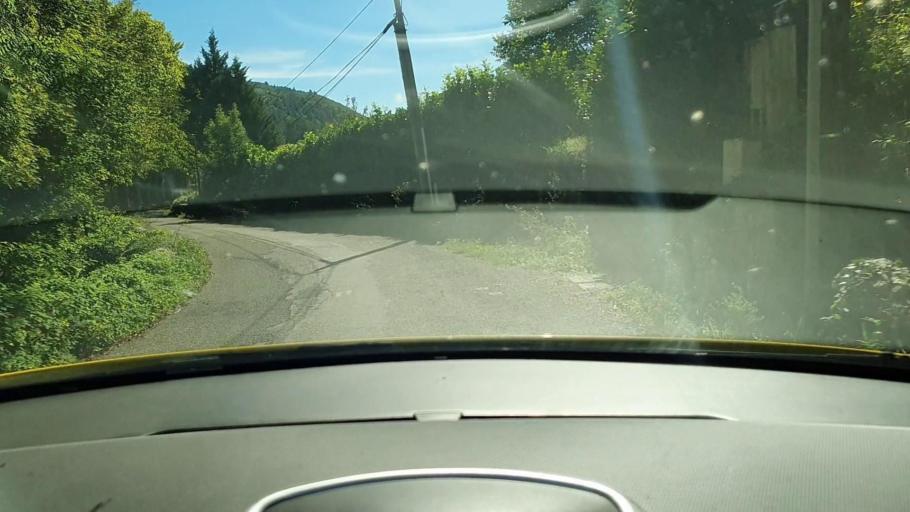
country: FR
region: Languedoc-Roussillon
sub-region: Departement du Gard
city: Le Vigan
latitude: 43.9703
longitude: 3.4375
